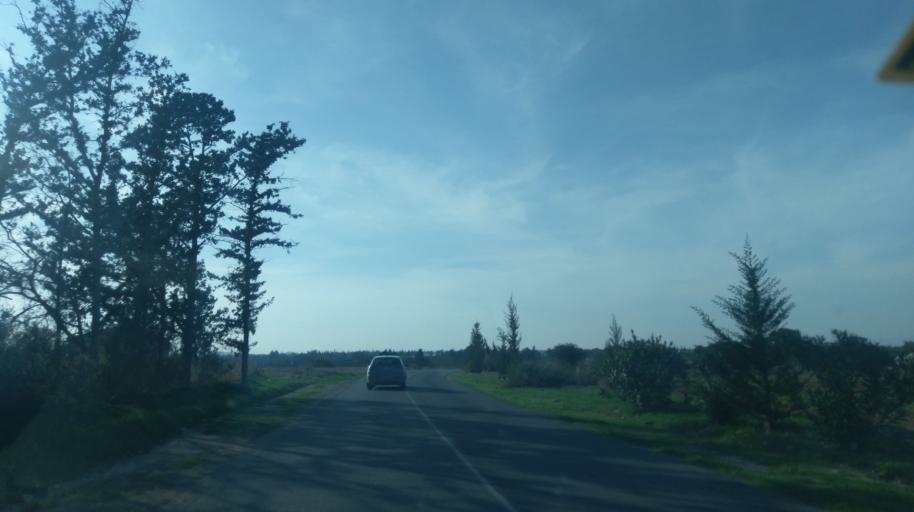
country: CY
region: Ammochostos
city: Achna
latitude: 35.1095
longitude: 33.7451
